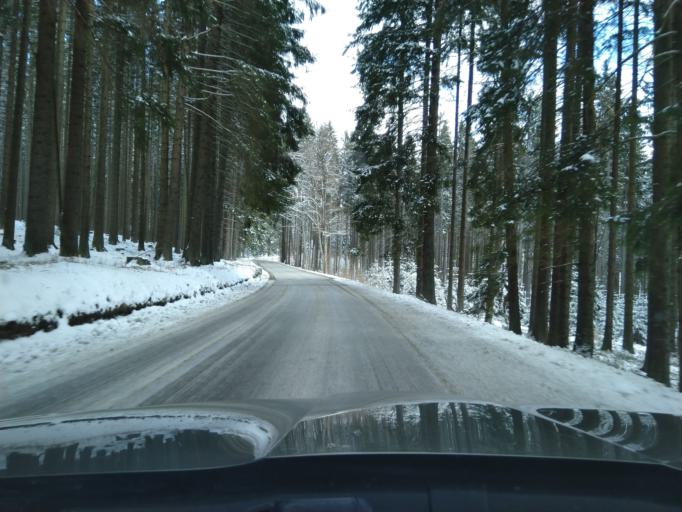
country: CZ
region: Jihocesky
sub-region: Okres Prachatice
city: Zdikov
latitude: 49.0498
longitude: 13.6882
